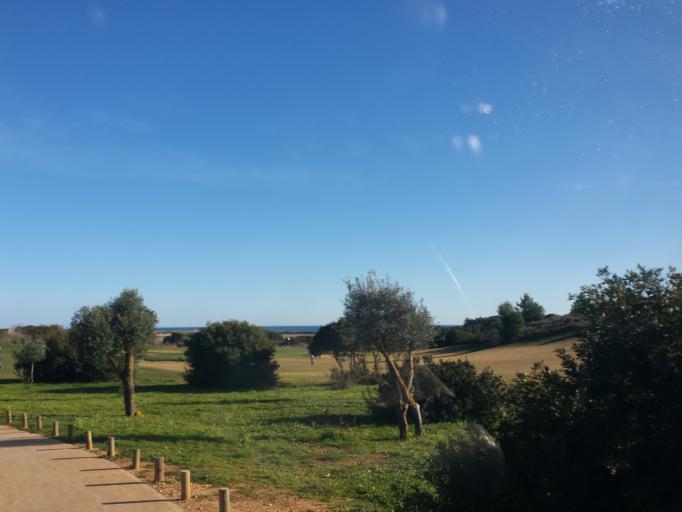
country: PT
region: Faro
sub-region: Portimao
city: Alvor
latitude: 37.1320
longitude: -8.6341
